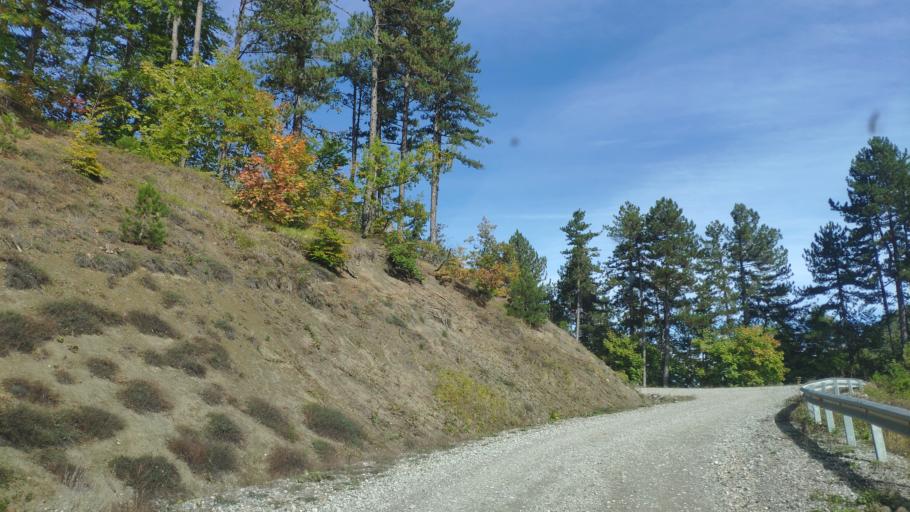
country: AL
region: Korce
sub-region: Rrethi i Devollit
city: Miras
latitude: 40.4187
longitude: 20.8699
